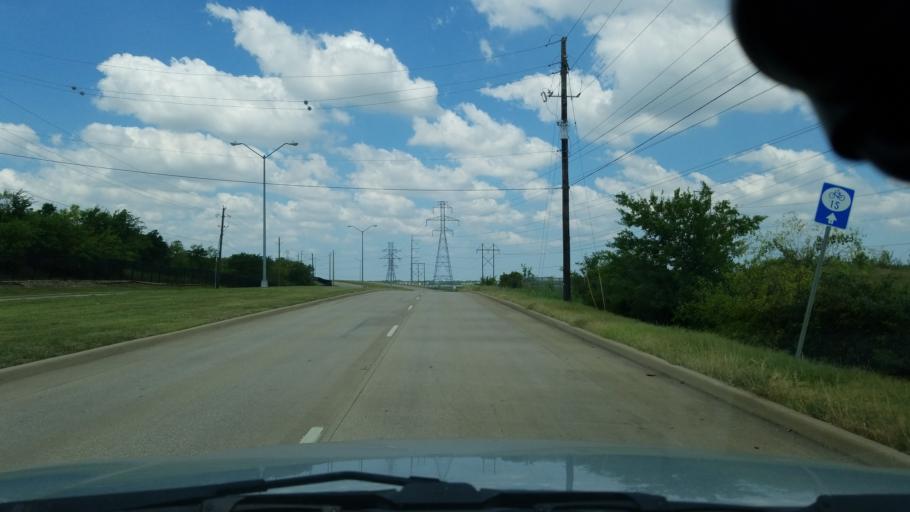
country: US
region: Texas
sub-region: Dallas County
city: Cockrell Hill
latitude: 32.7206
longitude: -96.9391
